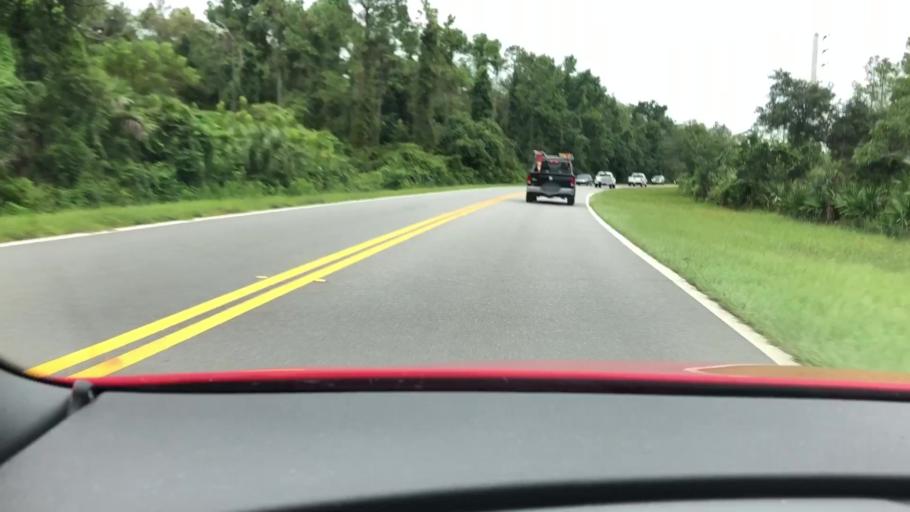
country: US
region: Florida
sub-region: Flagler County
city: Palm Coast
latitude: 29.5369
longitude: -81.2053
